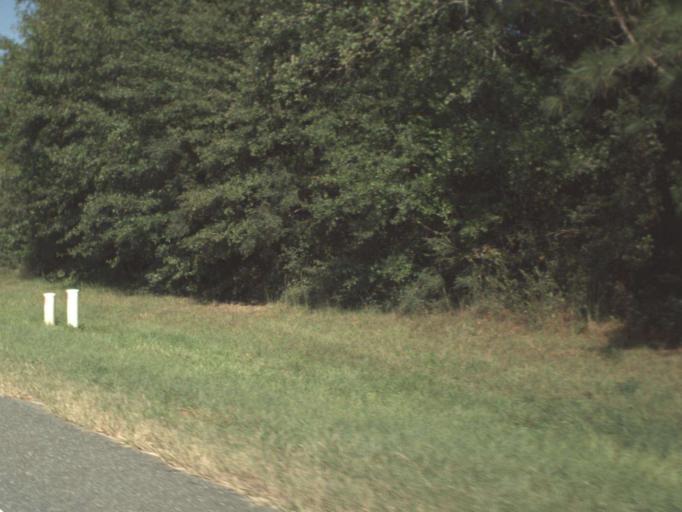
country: US
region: Florida
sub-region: Okaloosa County
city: Crestview
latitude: 30.8494
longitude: -86.5286
